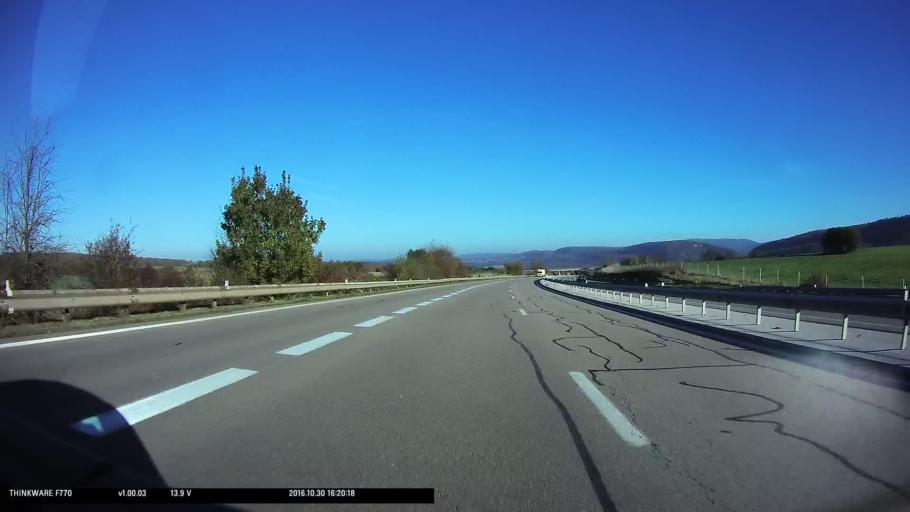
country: FR
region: Franche-Comte
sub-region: Departement du Doubs
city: Clerval
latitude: 47.4079
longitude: 6.4554
